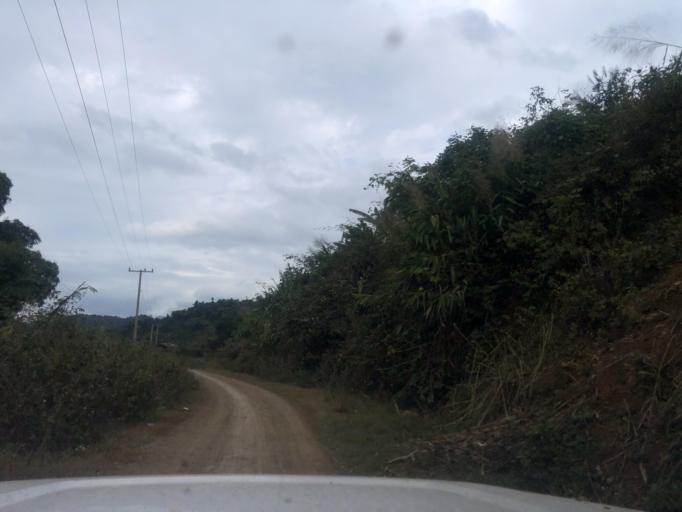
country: LA
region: Phongsali
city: Khoa
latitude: 21.2952
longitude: 102.5871
